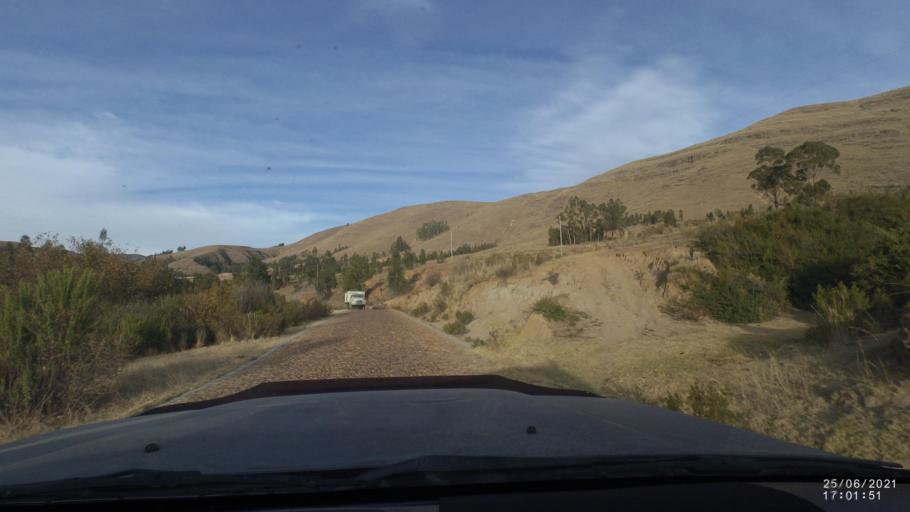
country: BO
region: Cochabamba
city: Arani
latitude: -17.8376
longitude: -65.7376
